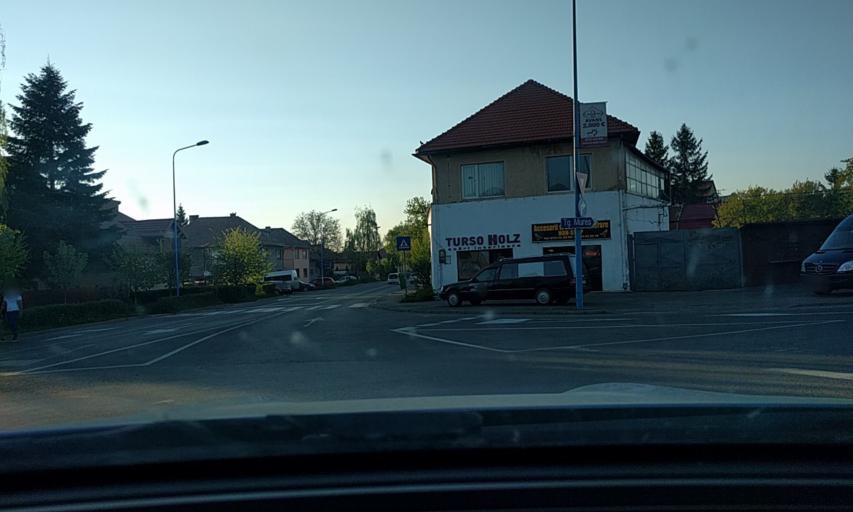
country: RO
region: Brasov
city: Brasov
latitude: 45.6668
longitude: 25.5776
